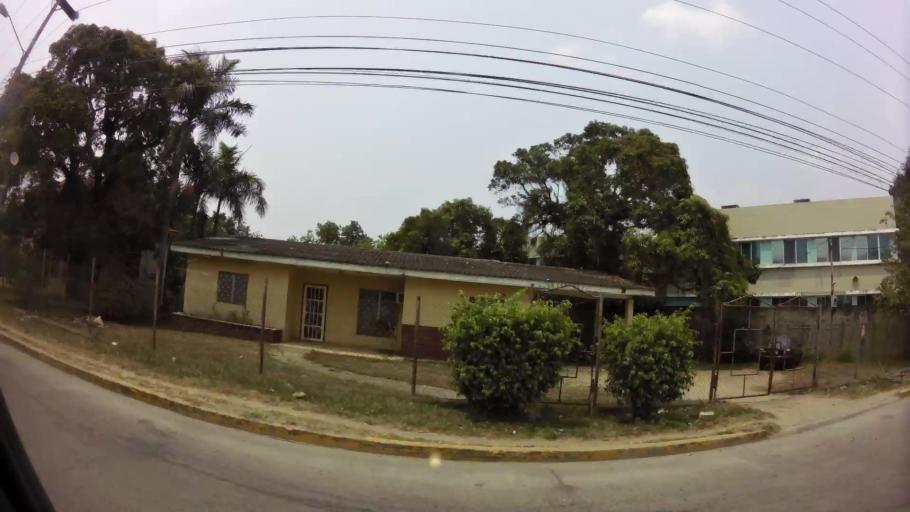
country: HN
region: Yoro
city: El Progreso
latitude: 15.3955
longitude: -87.8115
